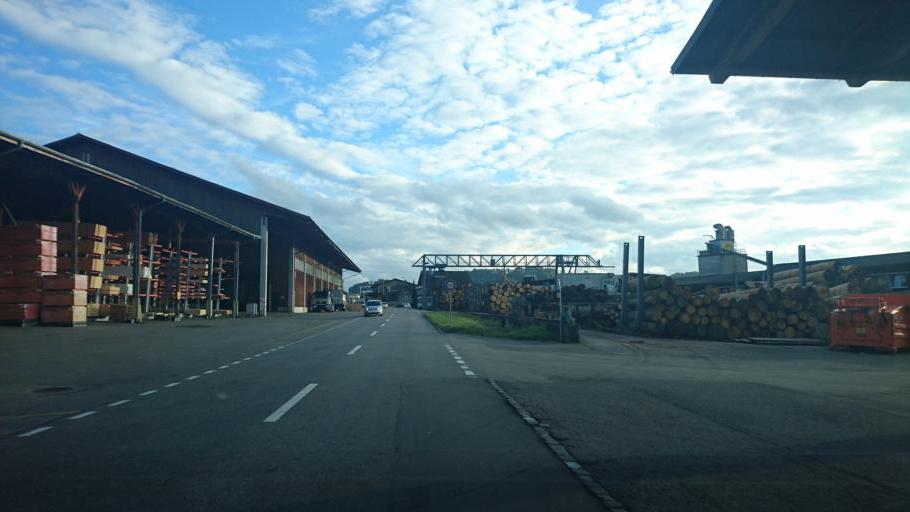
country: CH
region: Bern
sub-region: Bern-Mittelland District
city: Vechigen
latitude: 46.9414
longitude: 7.5576
